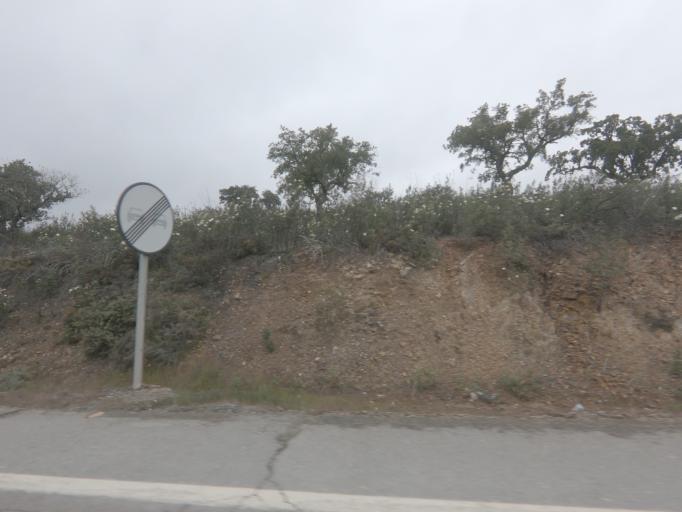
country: ES
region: Extremadura
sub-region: Provincia de Caceres
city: Malpartida de Caceres
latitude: 39.3011
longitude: -6.5160
